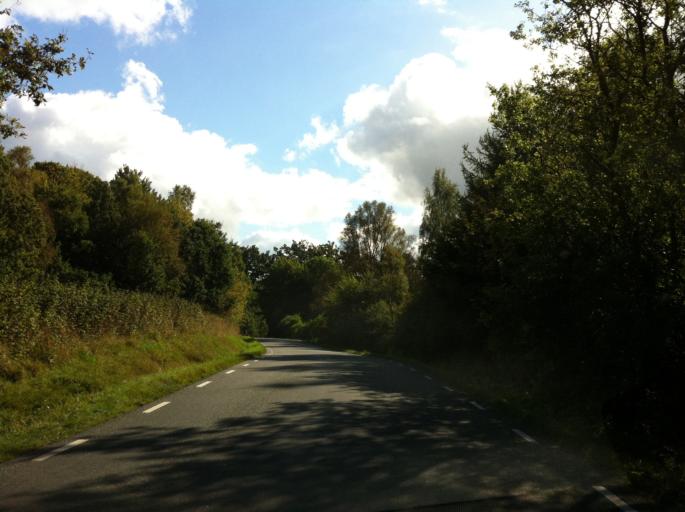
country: SE
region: Skane
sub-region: Kristianstads Kommun
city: Degeberga
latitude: 55.7394
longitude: 13.9379
